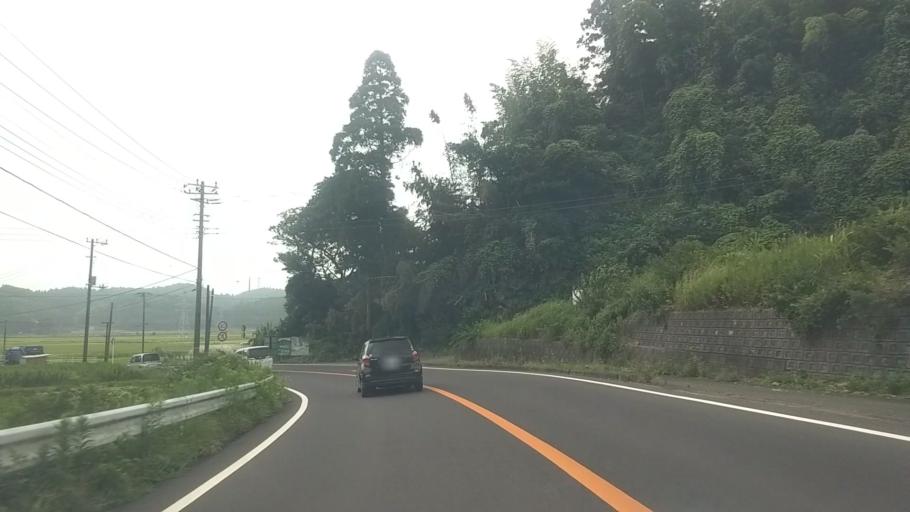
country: JP
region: Chiba
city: Ohara
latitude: 35.2644
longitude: 140.3717
